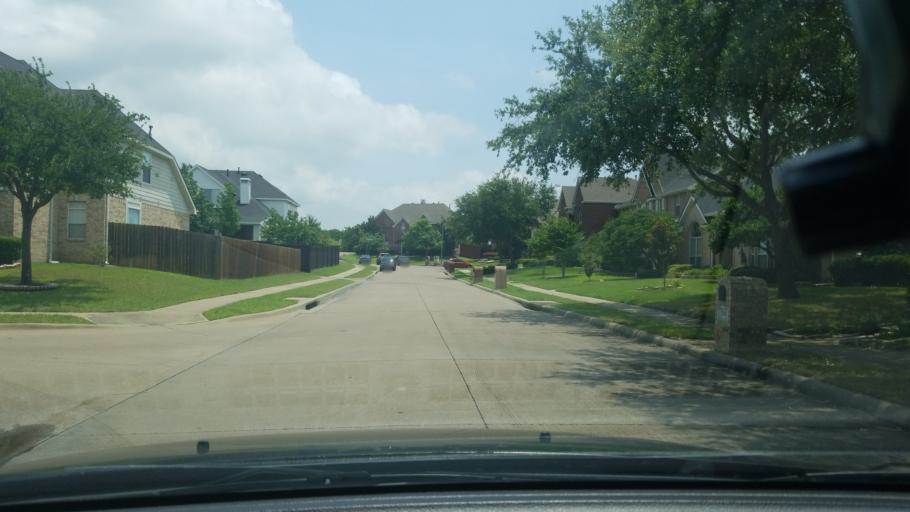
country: US
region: Texas
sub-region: Dallas County
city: Sunnyvale
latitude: 32.8099
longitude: -96.6012
